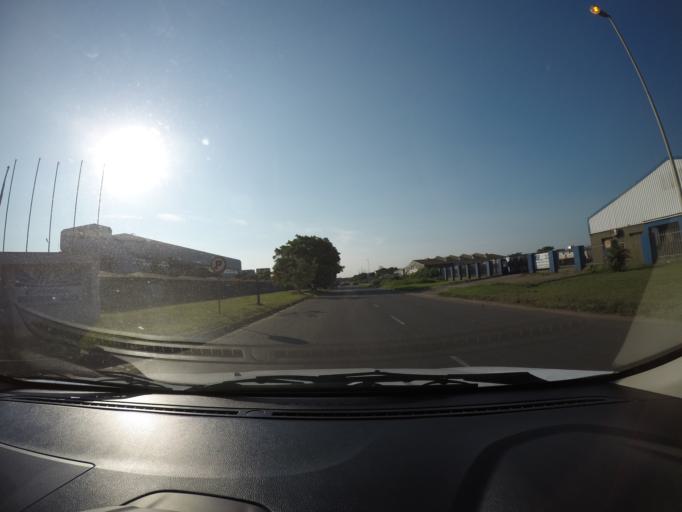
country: ZA
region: KwaZulu-Natal
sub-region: uThungulu District Municipality
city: Richards Bay
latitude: -28.7525
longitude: 32.0212
